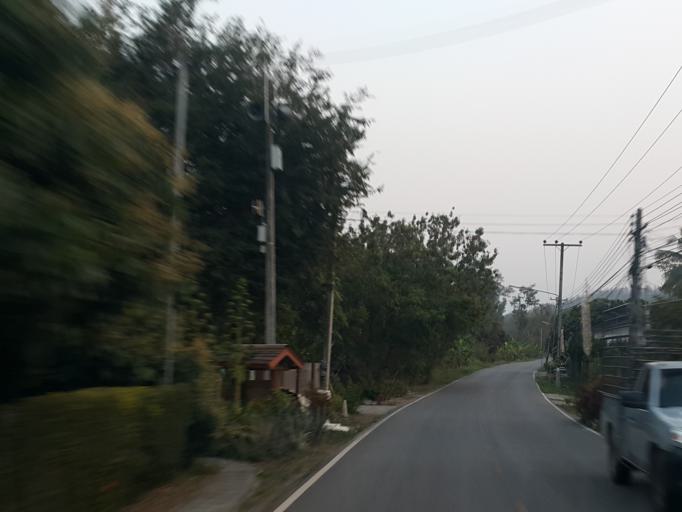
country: TH
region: Chiang Mai
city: Mae Taeng
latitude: 19.0106
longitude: 98.8854
